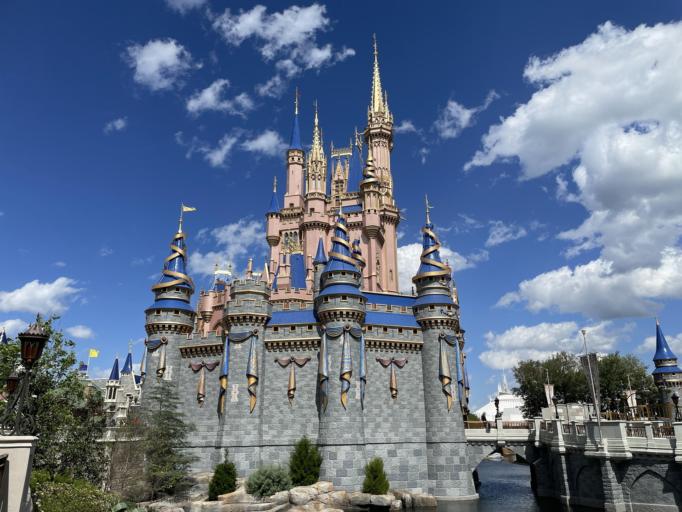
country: US
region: Florida
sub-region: Orange County
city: Bay Hill
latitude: 28.4194
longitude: -81.5817
